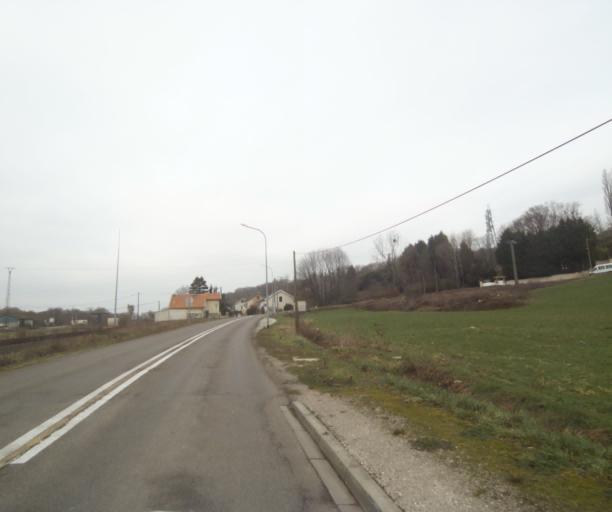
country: FR
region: Lorraine
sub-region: Departement de la Meuse
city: Ancerville
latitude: 48.6274
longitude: 4.9942
